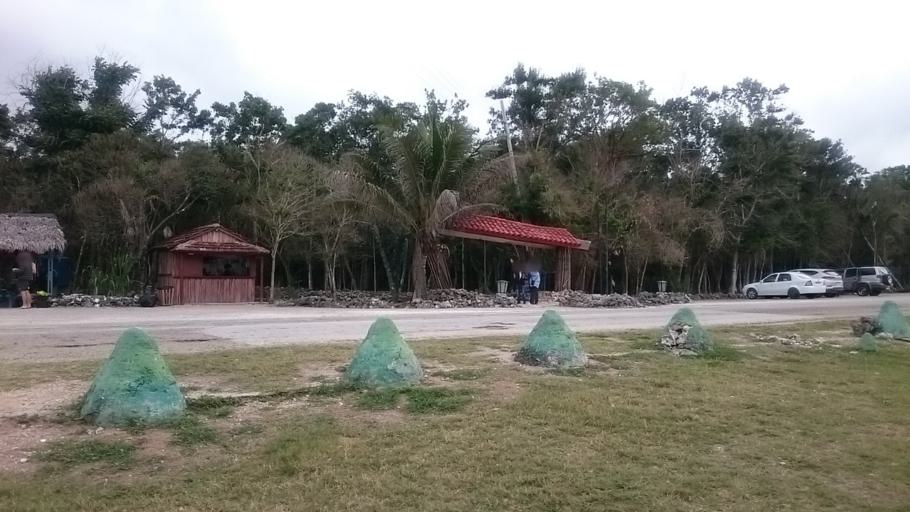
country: CU
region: Matanzas
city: Jaguey Grande
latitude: 22.1665
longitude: -81.1376
